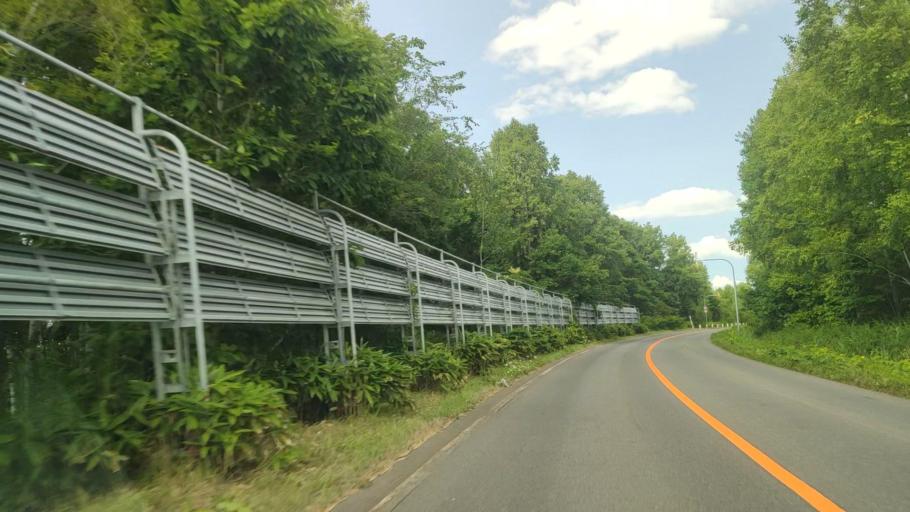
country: JP
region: Hokkaido
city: Nayoro
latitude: 44.2489
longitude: 142.4159
